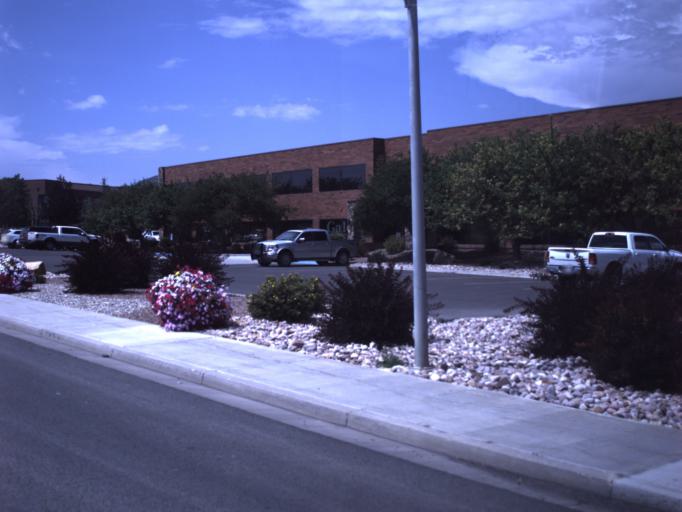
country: US
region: Utah
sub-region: Uintah County
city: Vernal
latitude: 40.4431
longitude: -109.5601
